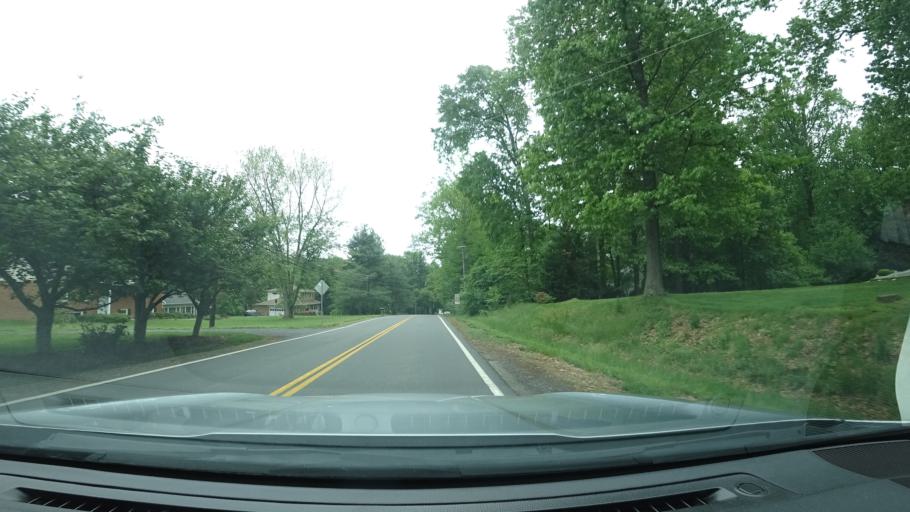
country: US
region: Virginia
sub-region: Fairfax County
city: Oakton
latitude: 38.8900
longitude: -77.3475
